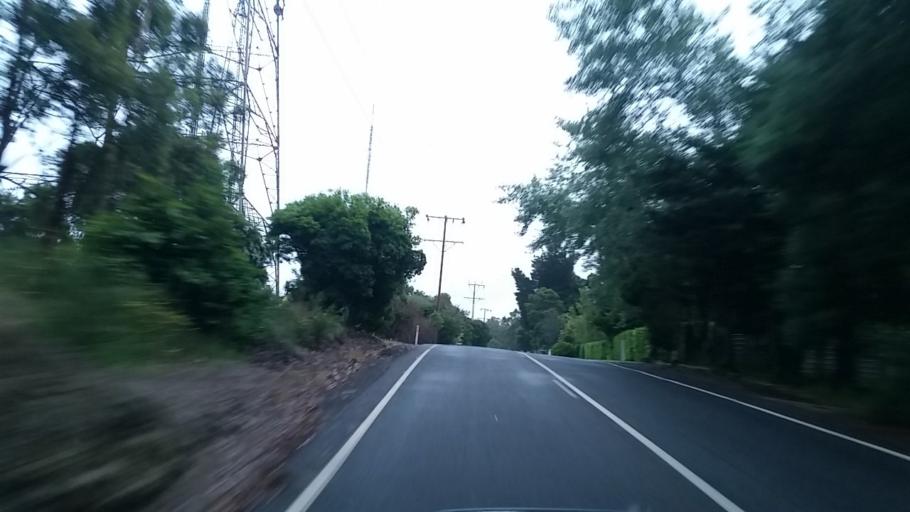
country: AU
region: South Australia
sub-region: Adelaide Hills
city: Crafers
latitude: -34.9831
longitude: 138.7085
